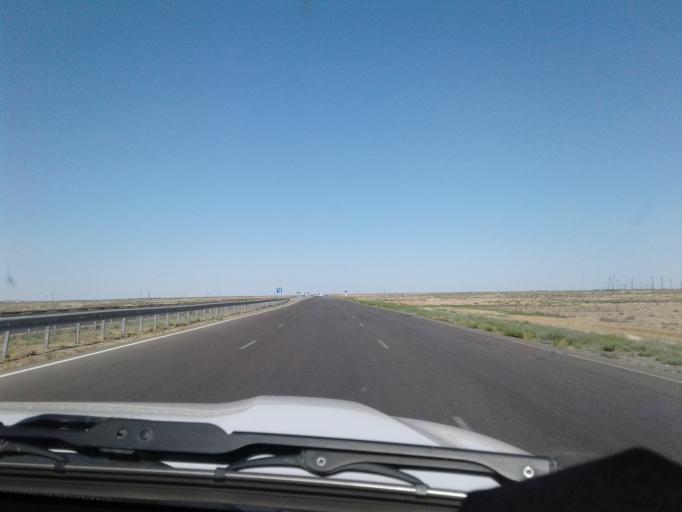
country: IR
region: Razavi Khorasan
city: Dargaz
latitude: 37.5912
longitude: 59.2449
